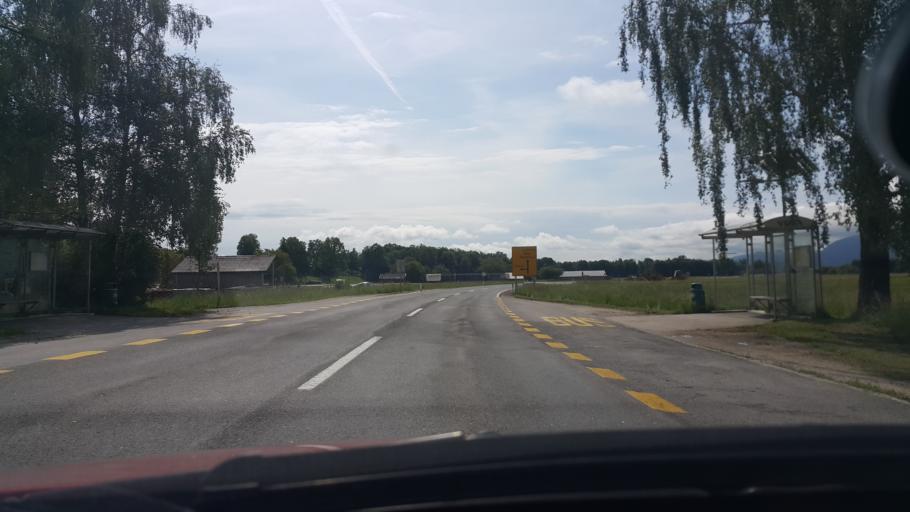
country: SI
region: Zirovnica
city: Zirovnica
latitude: 46.3877
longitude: 14.1452
